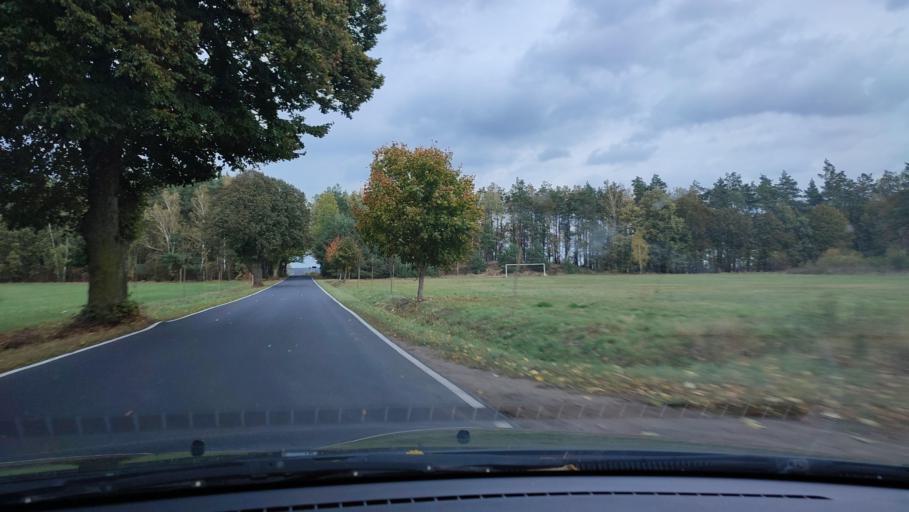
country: PL
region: Masovian Voivodeship
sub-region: Powiat mlawski
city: Wieczfnia Koscielna
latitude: 53.2167
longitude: 20.4060
